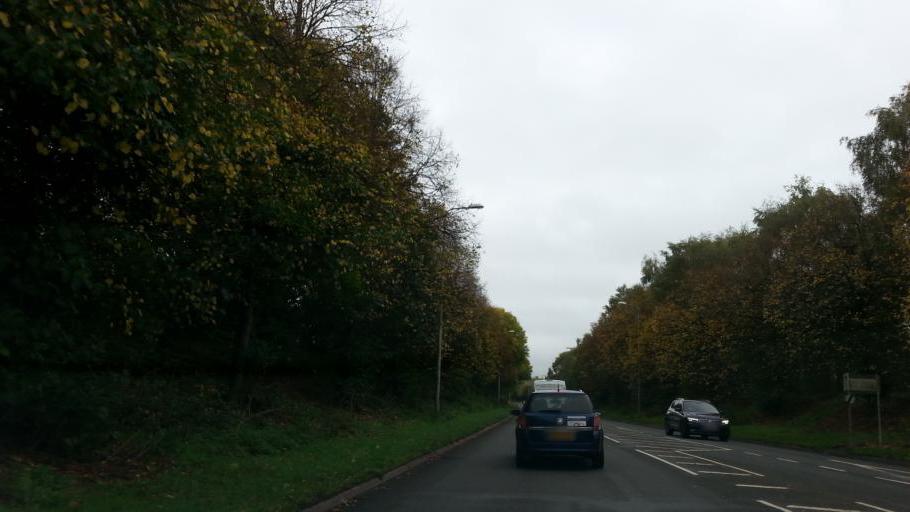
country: GB
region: England
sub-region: Worcestershire
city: Bromsgrove
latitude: 52.3305
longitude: -2.0523
